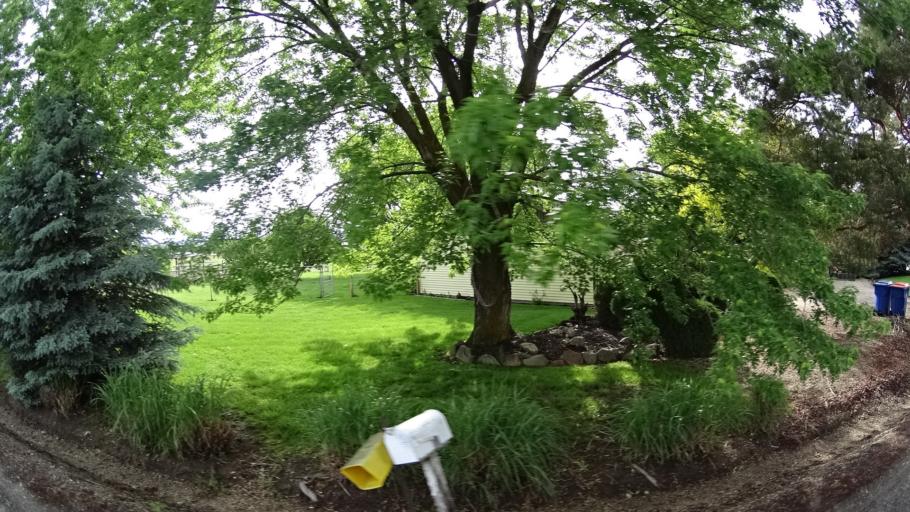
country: US
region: Idaho
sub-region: Ada County
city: Eagle
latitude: 43.7212
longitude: -116.4134
